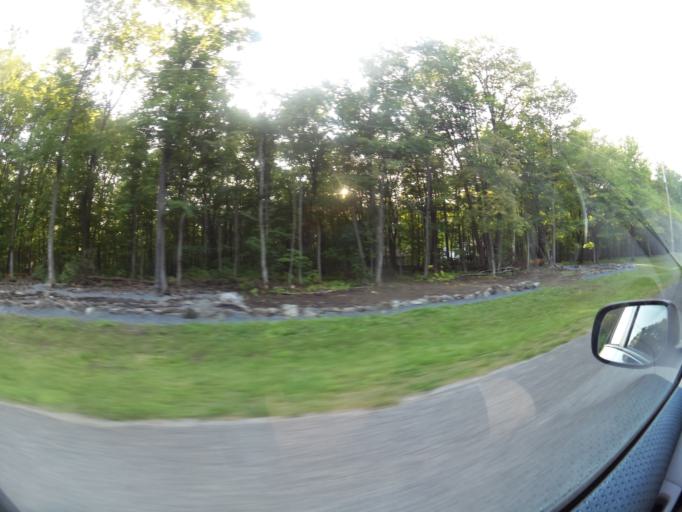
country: CA
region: Ontario
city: Clarence-Rockland
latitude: 45.5039
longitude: -75.4148
